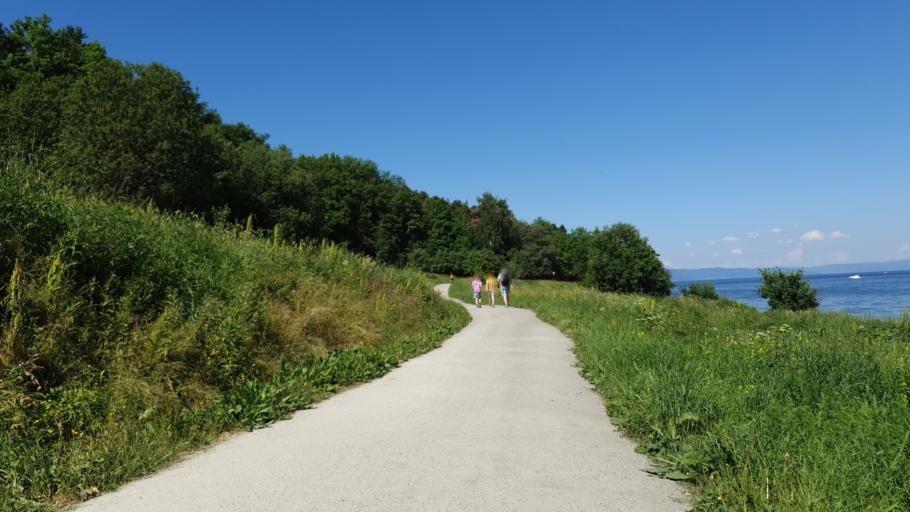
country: NO
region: Sor-Trondelag
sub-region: Trondheim
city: Trondheim
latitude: 63.4410
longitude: 10.4704
